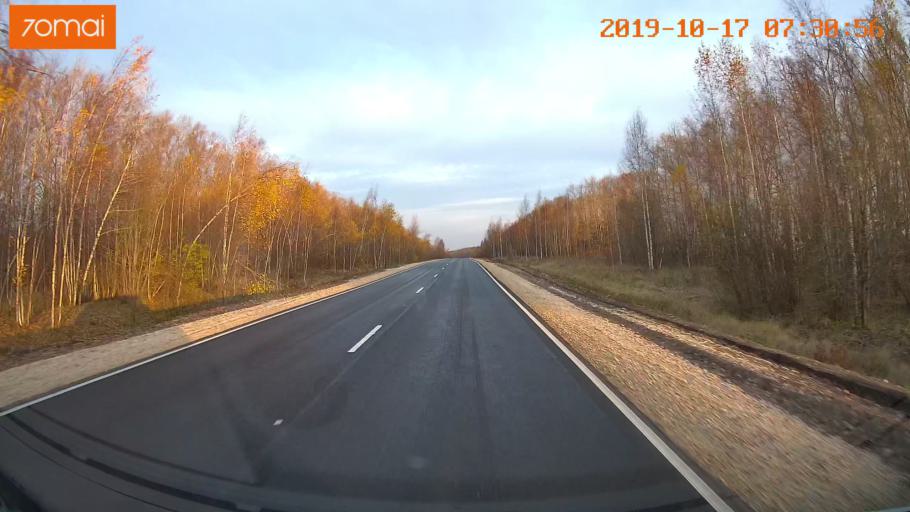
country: RU
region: Ivanovo
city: Gavrilov Posad
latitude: 56.3826
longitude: 40.0039
